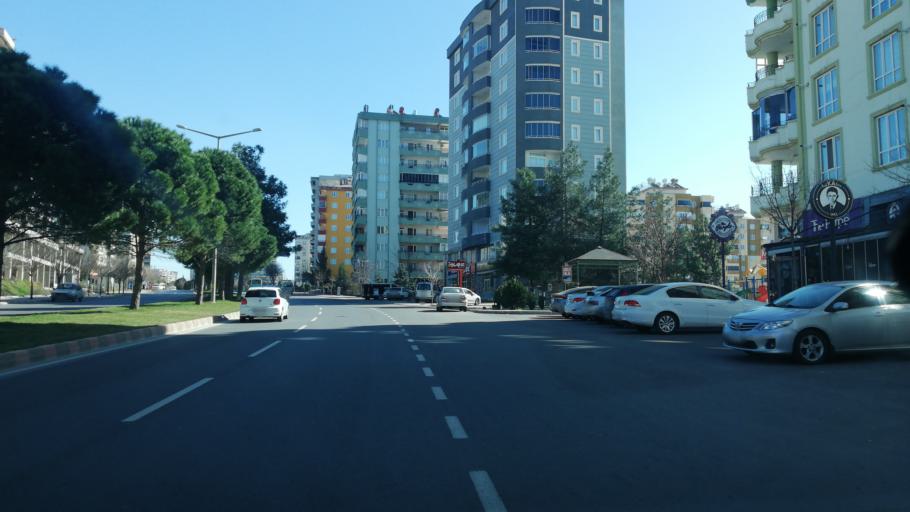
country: TR
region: Kahramanmaras
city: Kahramanmaras
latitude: 37.5828
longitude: 36.8813
